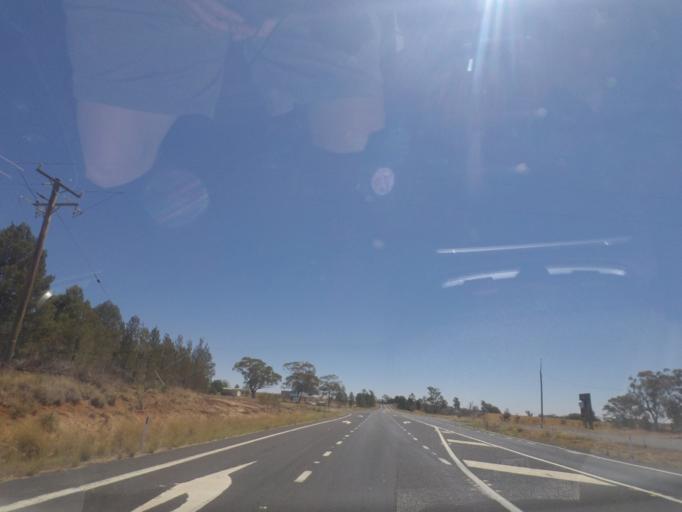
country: AU
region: New South Wales
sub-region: Gilgandra
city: Gilgandra
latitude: -31.4694
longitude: 148.9211
